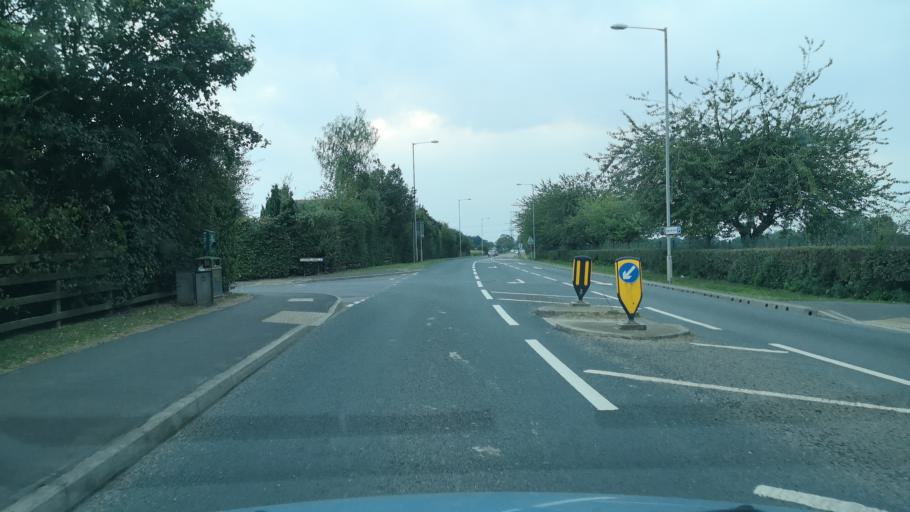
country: GB
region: England
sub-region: East Riding of Yorkshire
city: Snaith
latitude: 53.6890
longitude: -1.0372
